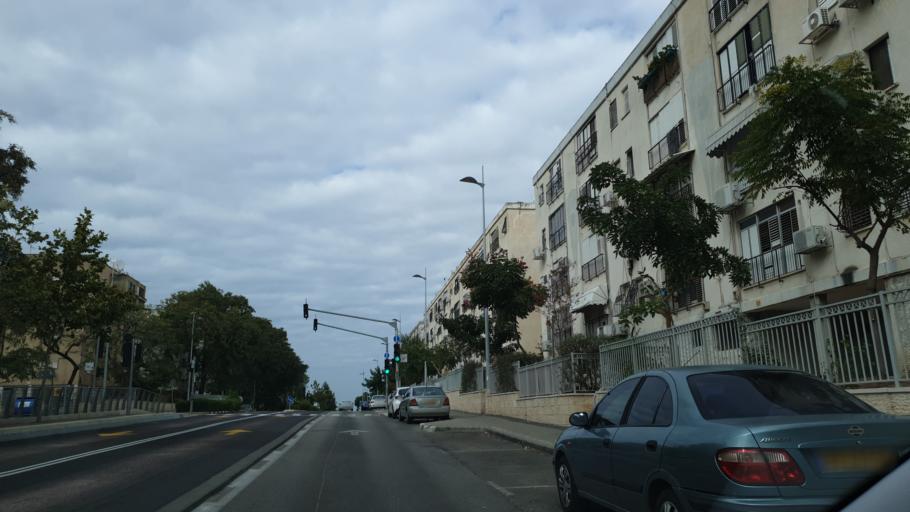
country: IL
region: Haifa
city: Qiryat Ata
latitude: 32.8086
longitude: 35.1171
